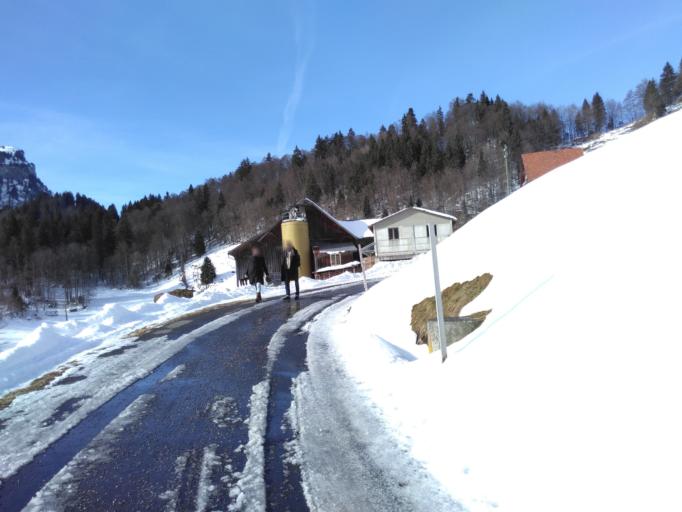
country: CH
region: Schwyz
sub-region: Bezirk March
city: Vorderthal
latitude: 47.1074
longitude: 8.9229
